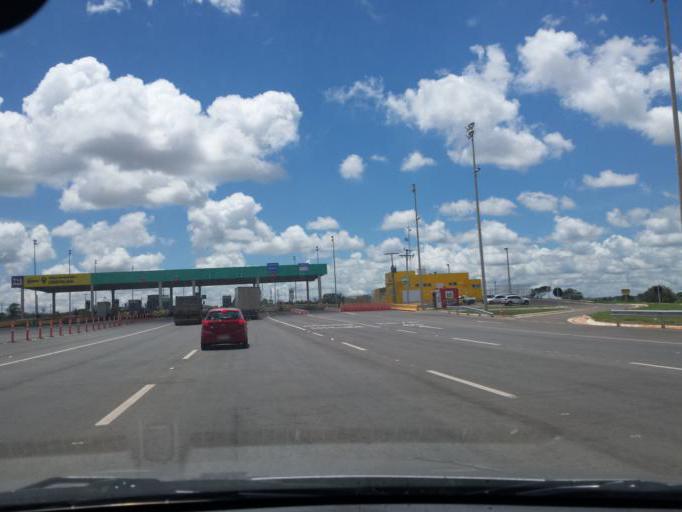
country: BR
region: Goias
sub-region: Cristalina
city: Cristalina
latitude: -16.7380
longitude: -47.6183
